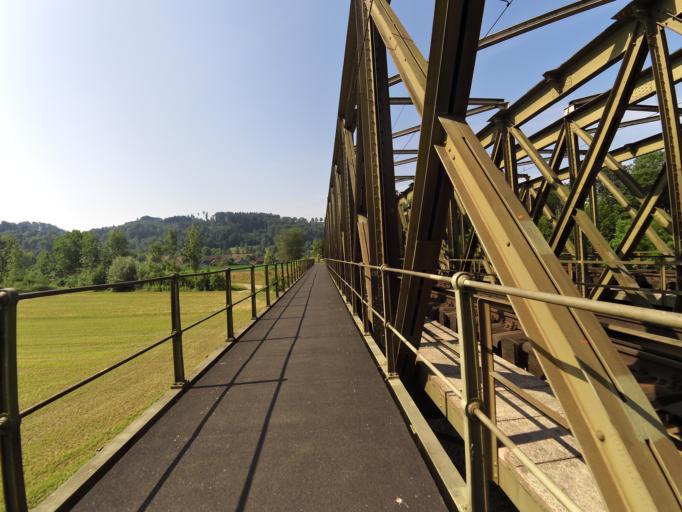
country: CH
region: Thurgau
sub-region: Frauenfeld District
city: Mullheim
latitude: 47.5841
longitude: 9.0068
